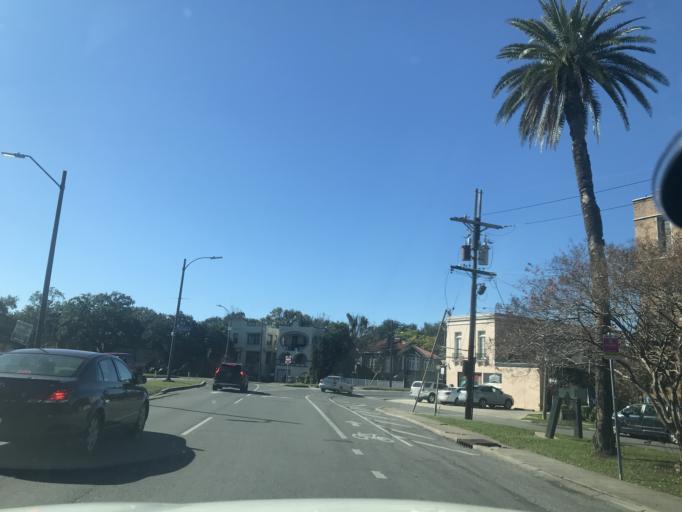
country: US
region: Louisiana
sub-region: Orleans Parish
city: New Orleans
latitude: 29.9493
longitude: -90.1038
